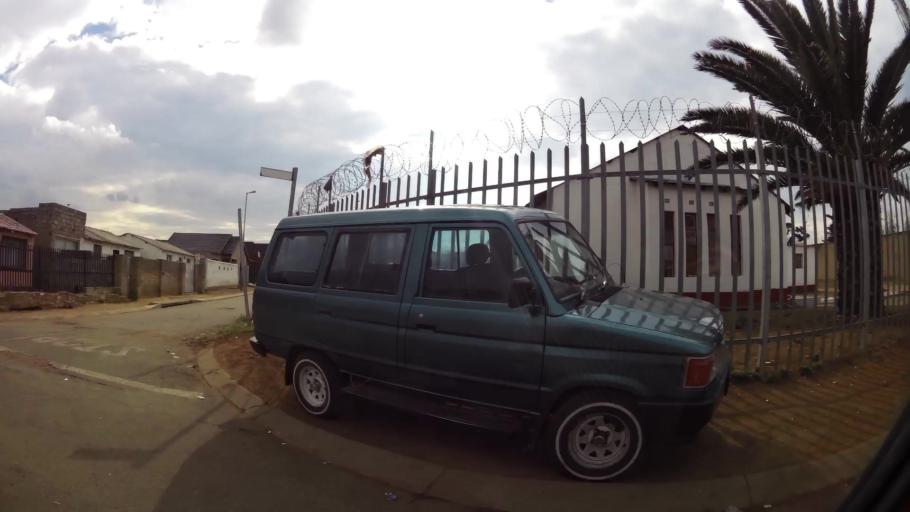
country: ZA
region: Gauteng
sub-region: City of Johannesburg Metropolitan Municipality
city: Soweto
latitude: -26.2374
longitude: 27.8647
